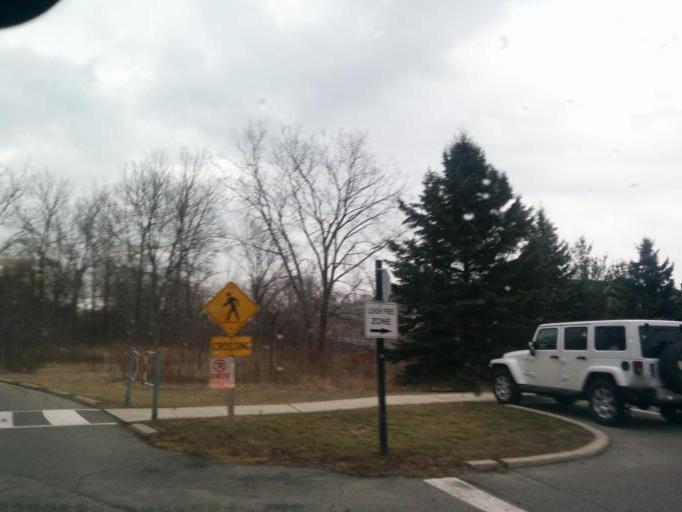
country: CA
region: Ontario
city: Mississauga
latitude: 43.5293
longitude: -79.6066
